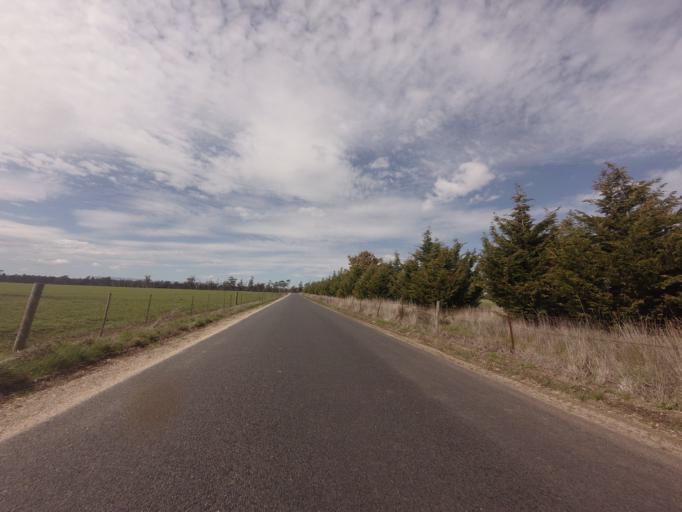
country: AU
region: Tasmania
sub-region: Northern Midlands
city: Longford
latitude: -41.6629
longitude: 147.1876
